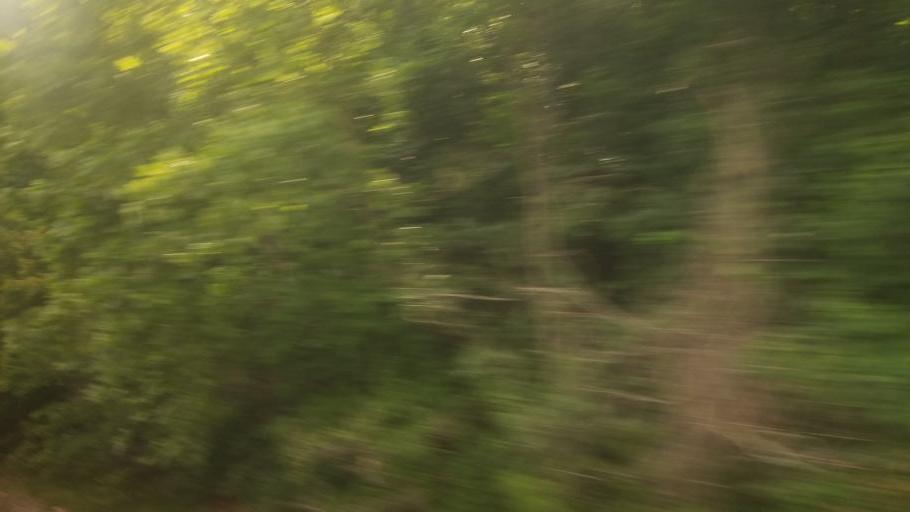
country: US
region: Kansas
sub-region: Johnson County
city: De Soto
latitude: 38.9824
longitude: -94.9182
